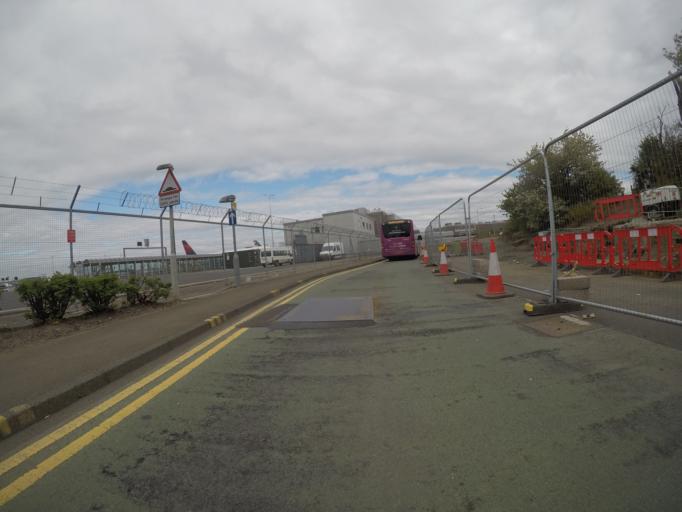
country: GB
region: Scotland
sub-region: Edinburgh
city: Ratho
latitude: 55.9458
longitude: -3.3650
